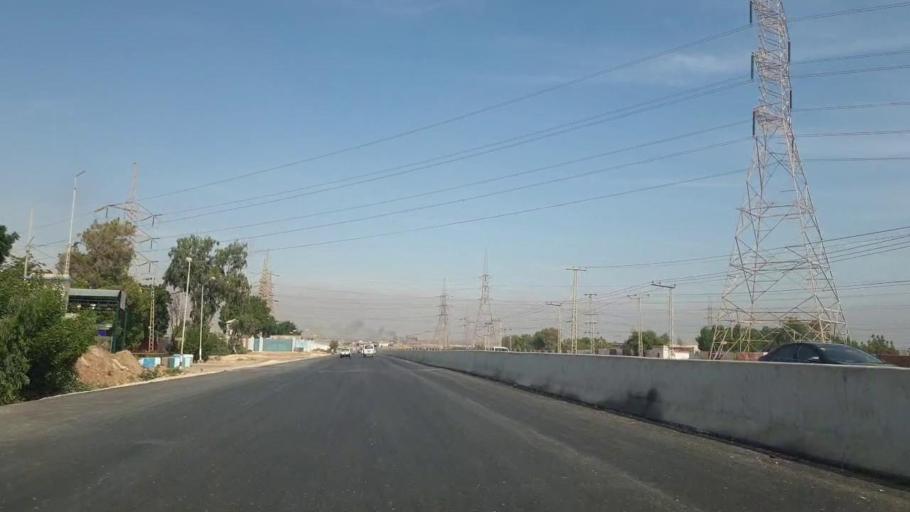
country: PK
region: Sindh
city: Jamshoro
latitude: 25.4743
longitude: 68.2709
